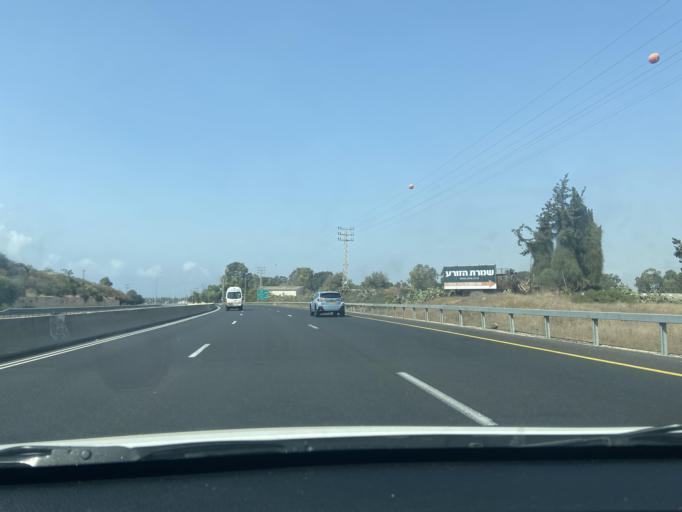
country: IL
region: Northern District
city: `Akko
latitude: 32.9447
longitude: 35.0954
